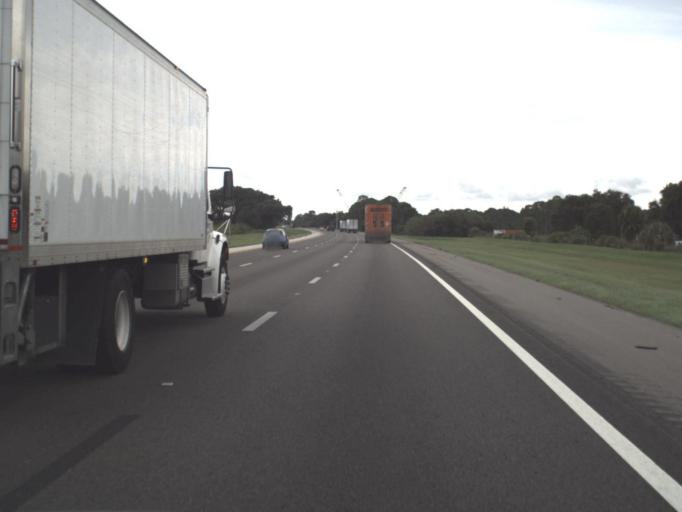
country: US
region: Florida
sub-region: Sarasota County
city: Laurel
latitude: 27.1696
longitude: -82.4333
